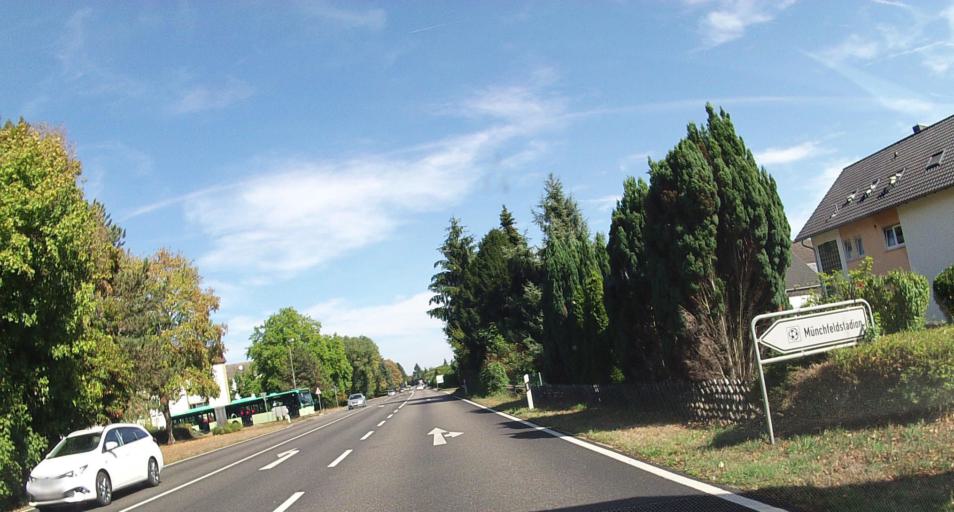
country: DE
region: Baden-Wuerttemberg
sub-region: Karlsruhe Region
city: Rastatt
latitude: 48.8347
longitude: 8.1996
